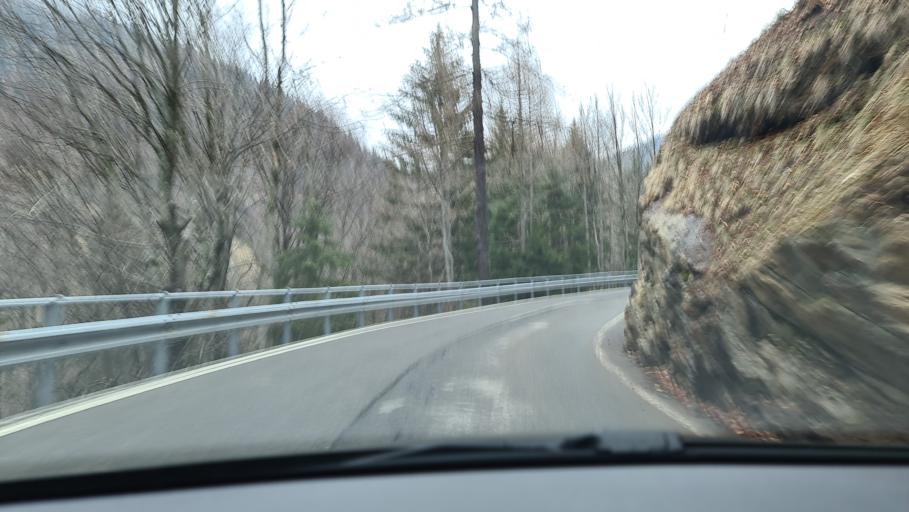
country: CH
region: Ticino
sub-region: Leventina District
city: Airolo
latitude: 46.4404
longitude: 8.6606
